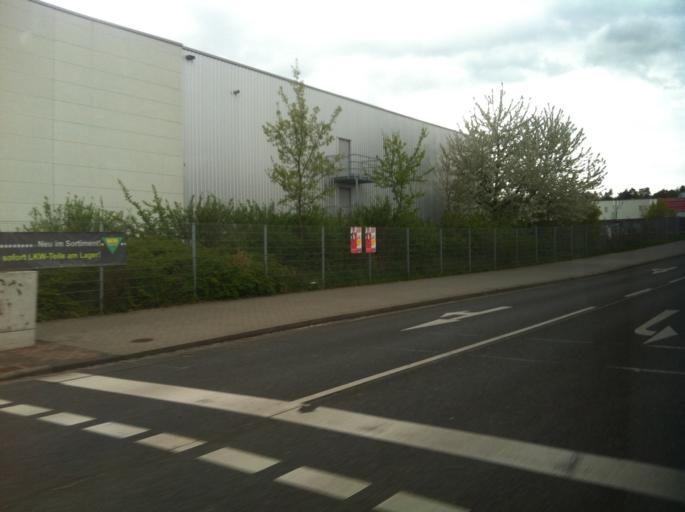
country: DE
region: Rheinland-Pfalz
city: Mainz
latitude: 49.9756
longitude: 8.2810
